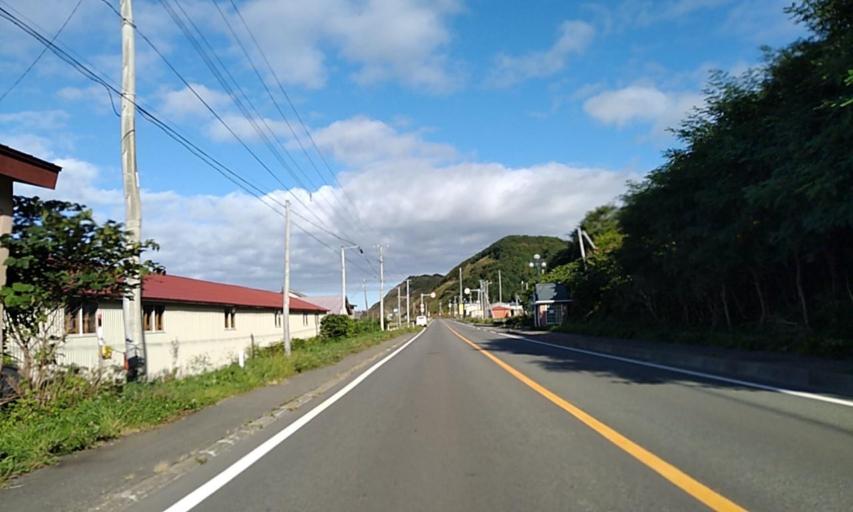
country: JP
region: Hokkaido
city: Shizunai-furukawacho
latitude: 42.2036
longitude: 142.6573
